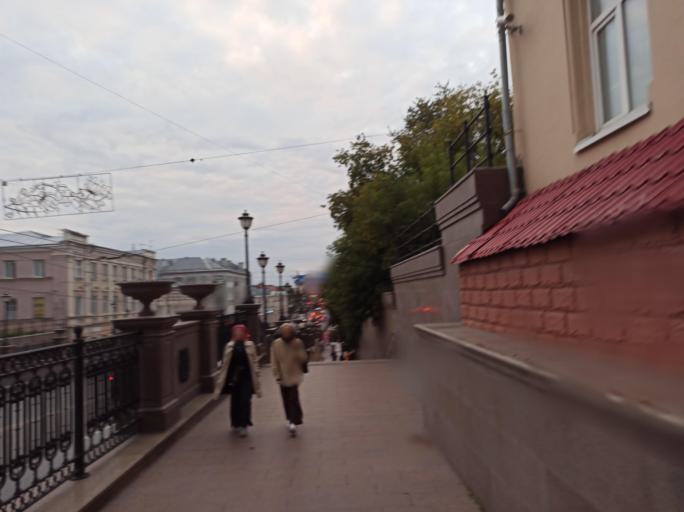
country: RU
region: Tomsk
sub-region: Tomskiy Rayon
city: Tomsk
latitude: 56.4806
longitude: 84.9495
